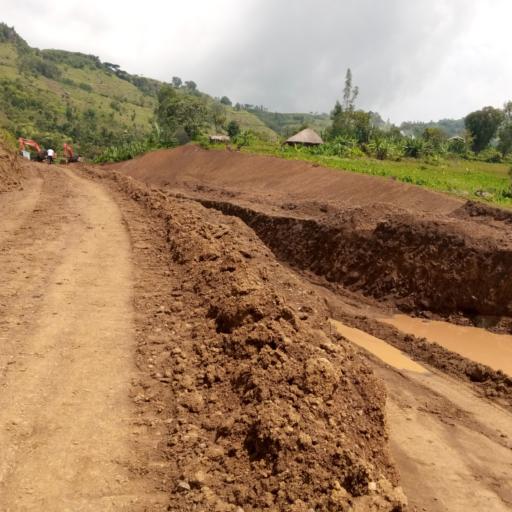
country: ET
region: Southern Nations, Nationalities, and People's Region
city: Arba Minch'
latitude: 6.3158
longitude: 37.3587
